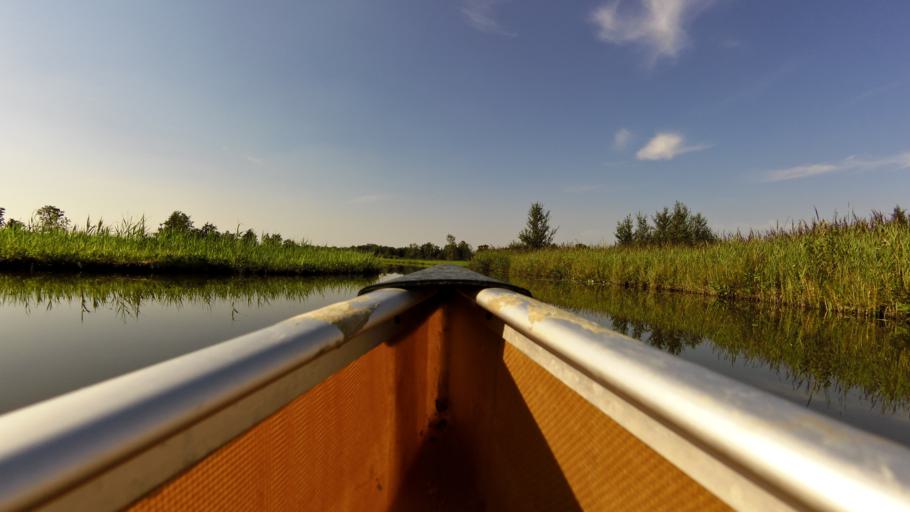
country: NL
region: South Holland
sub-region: Gemeente Nieuwkoop
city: Nieuwkoop
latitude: 52.1297
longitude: 4.7879
